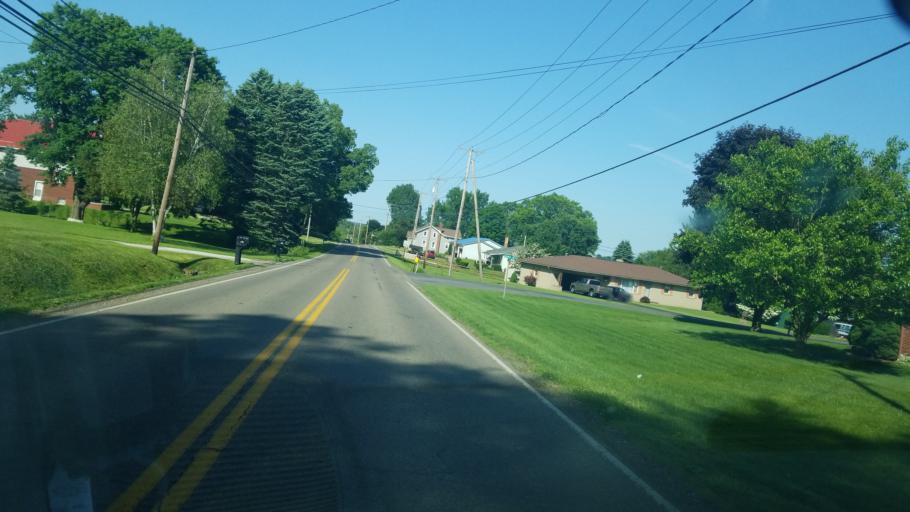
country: US
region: Ohio
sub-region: Wayne County
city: Wooster
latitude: 40.7828
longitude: -81.9570
